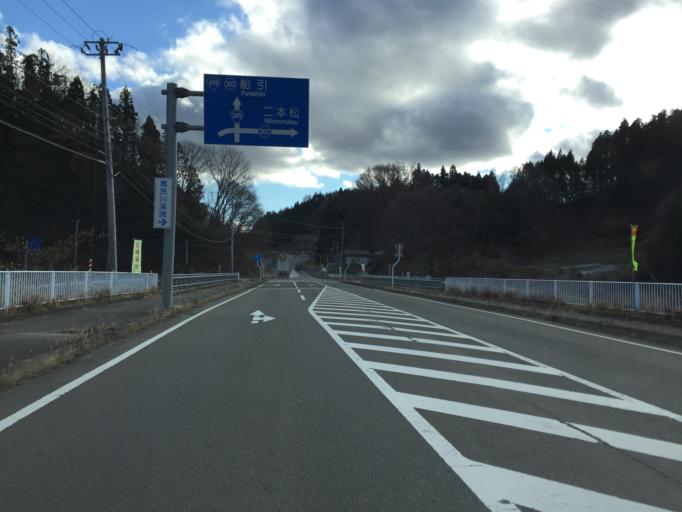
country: JP
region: Fukushima
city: Funehikimachi-funehiki
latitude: 37.5657
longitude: 140.5778
